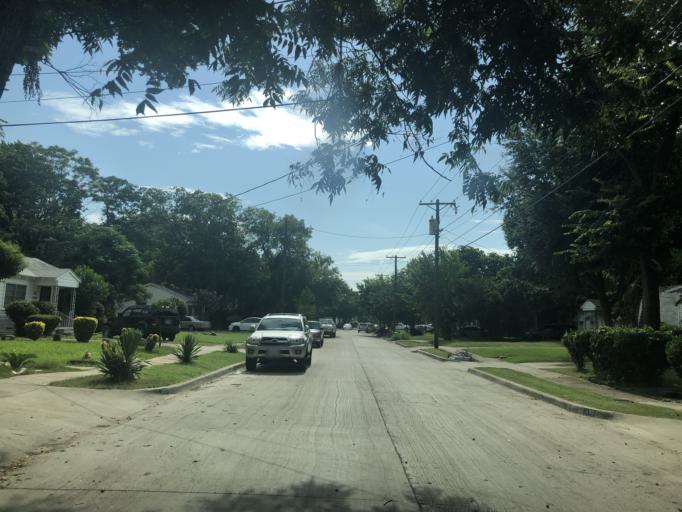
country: US
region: Texas
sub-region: Dallas County
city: Dallas
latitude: 32.8139
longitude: -96.8563
